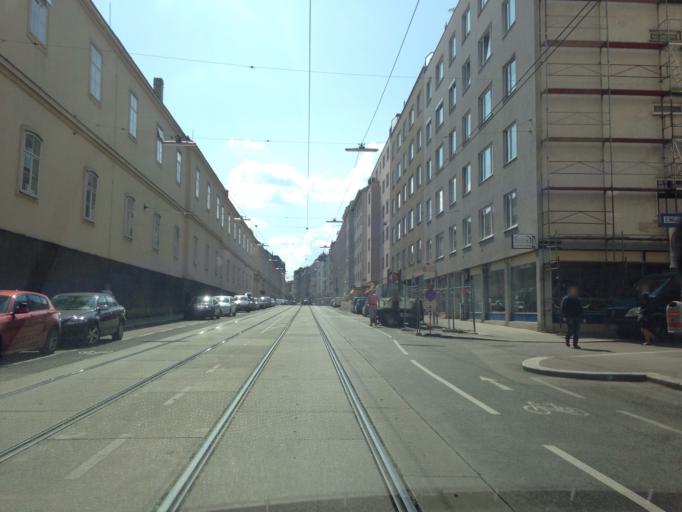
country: AT
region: Vienna
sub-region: Wien Stadt
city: Vienna
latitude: 48.2181
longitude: 16.3515
